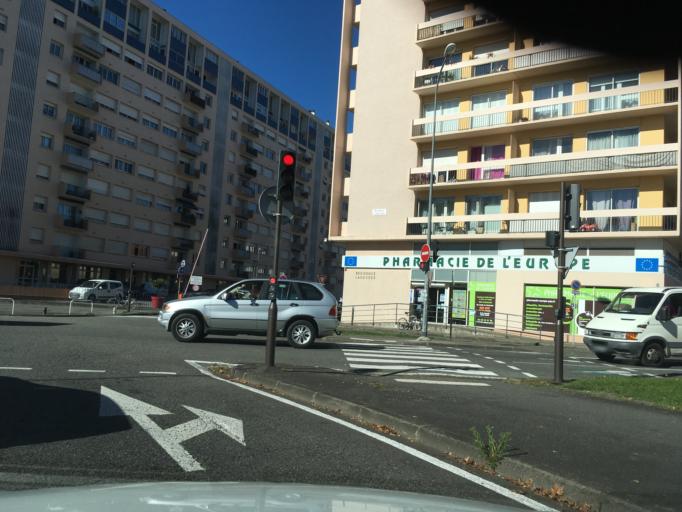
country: FR
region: Aquitaine
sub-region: Departement des Pyrenees-Atlantiques
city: Pau
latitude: 43.3060
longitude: -0.3763
